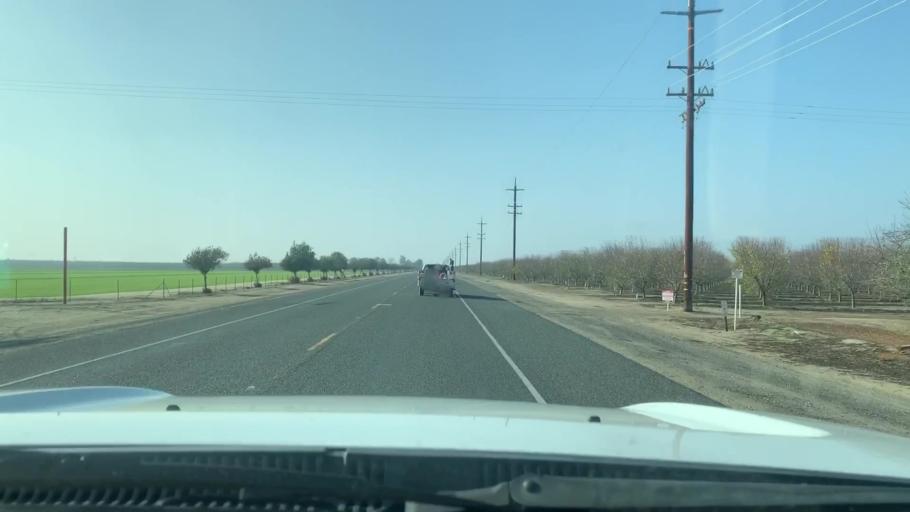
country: US
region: California
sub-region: Kern County
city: Wasco
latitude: 35.6015
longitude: -119.4112
